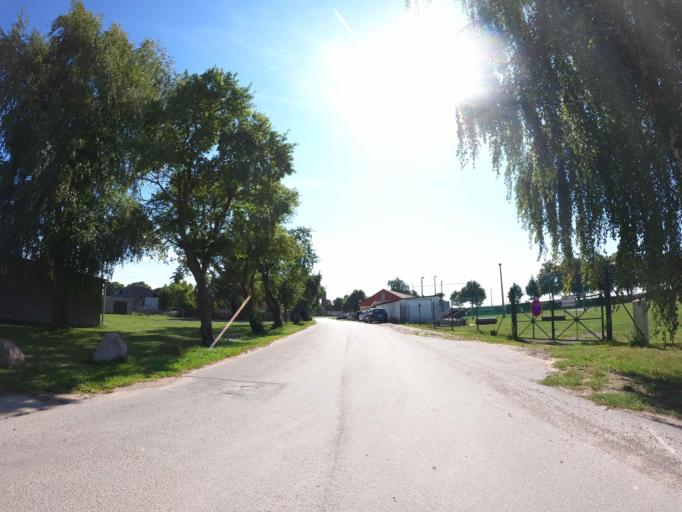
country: DE
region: Mecklenburg-Vorpommern
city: Prohn
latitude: 54.3783
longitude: 13.0219
